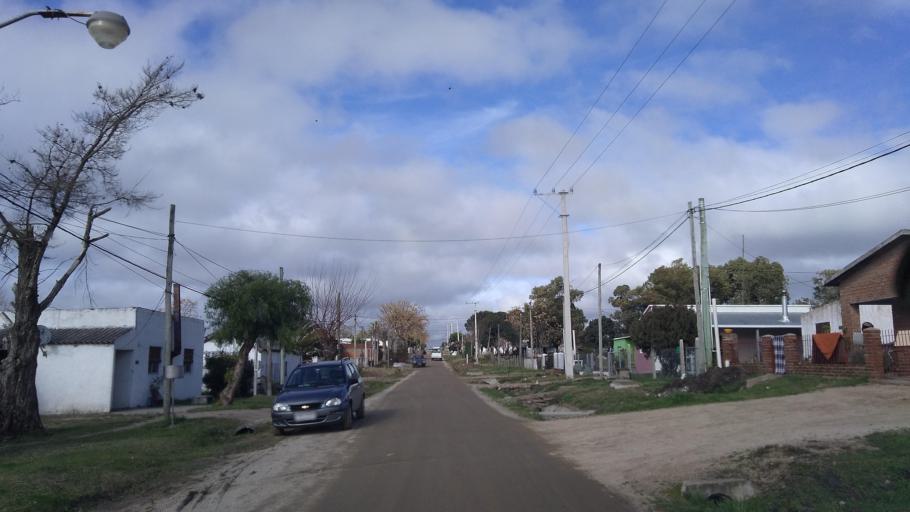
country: UY
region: Canelones
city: Tala
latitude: -34.1919
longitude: -55.7418
